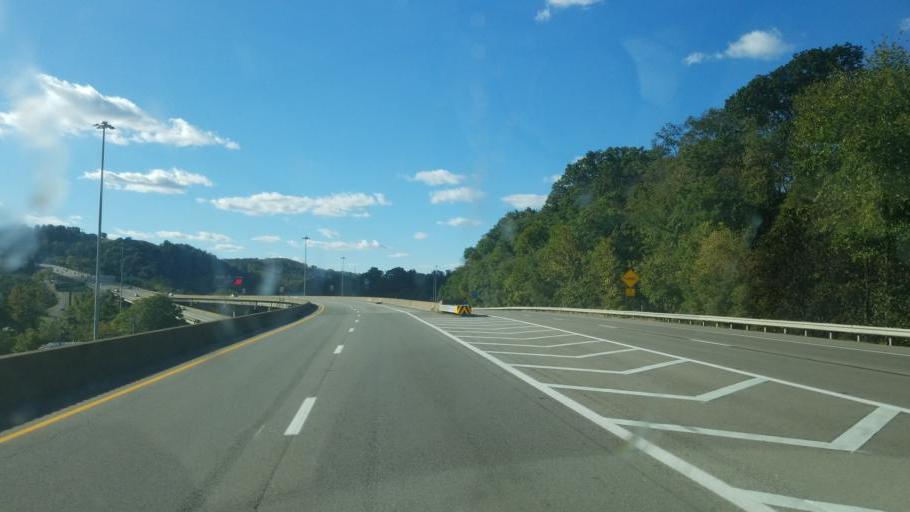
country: US
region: West Virginia
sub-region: Ohio County
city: Bethlehem
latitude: 40.0482
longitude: -80.6619
